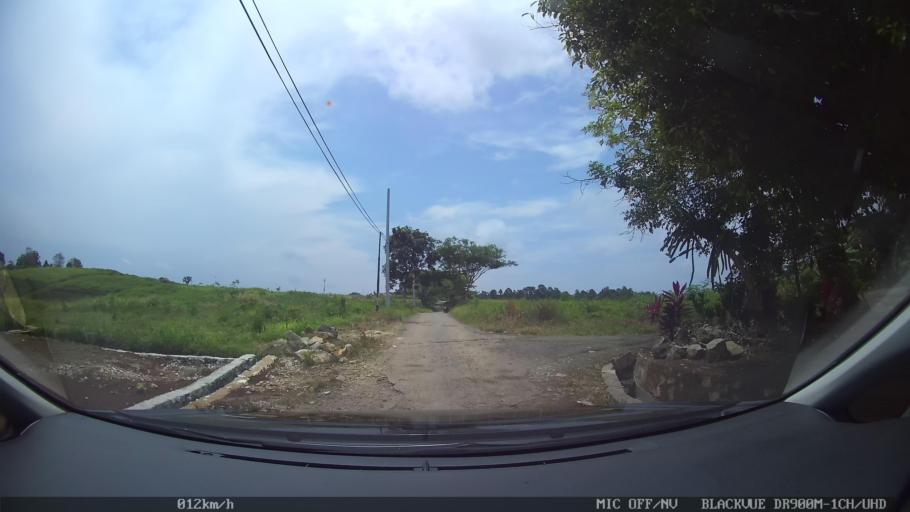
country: ID
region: Lampung
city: Bandarlampung
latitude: -5.4117
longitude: 105.2028
